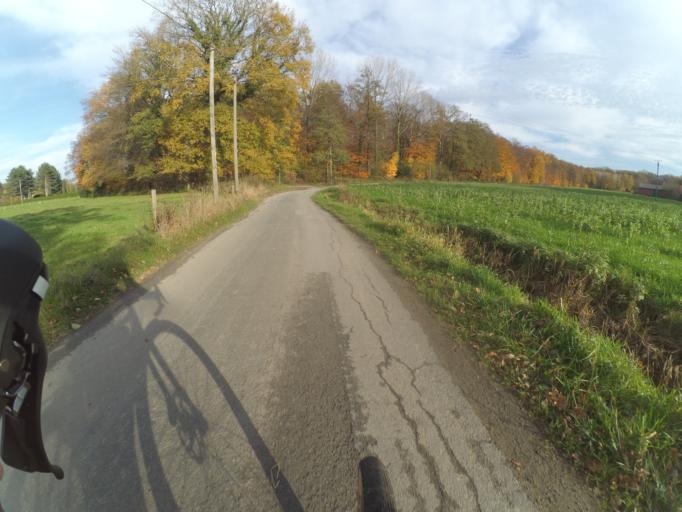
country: DE
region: North Rhine-Westphalia
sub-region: Regierungsbezirk Munster
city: Tecklenburg
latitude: 52.2336
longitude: 7.8057
